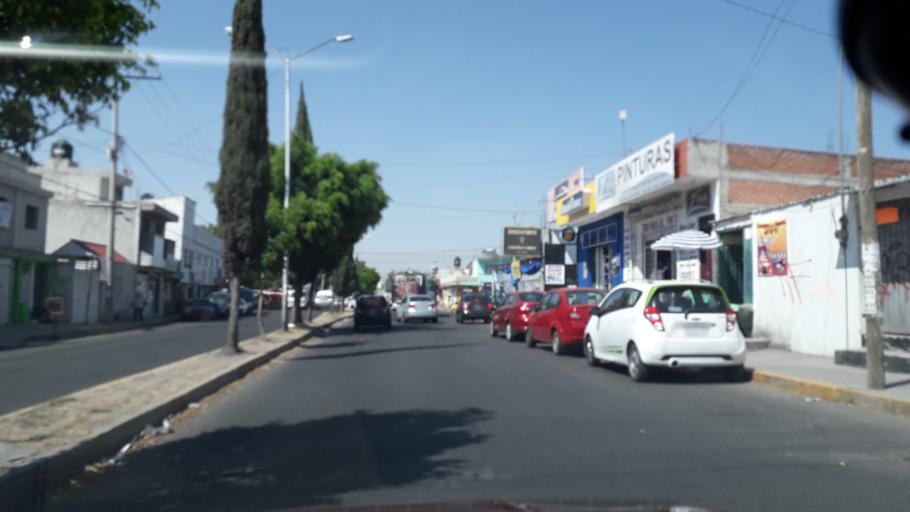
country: MX
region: Puebla
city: Puebla
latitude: 18.9902
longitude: -98.2144
